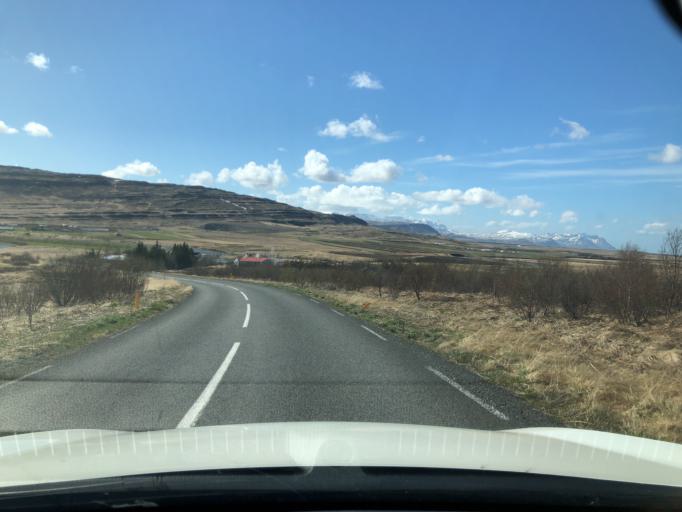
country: IS
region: West
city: Borgarnes
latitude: 64.6678
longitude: -21.4076
